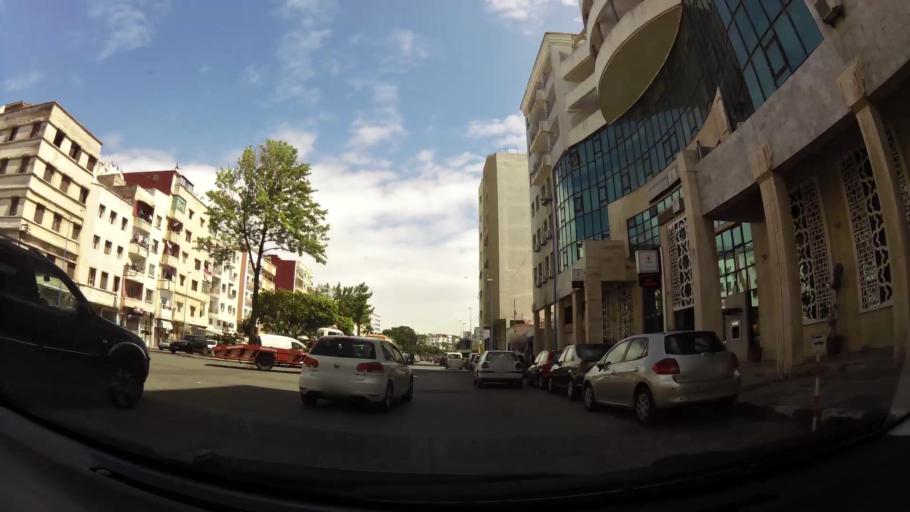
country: MA
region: Grand Casablanca
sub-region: Casablanca
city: Casablanca
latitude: 33.6001
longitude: -7.6363
